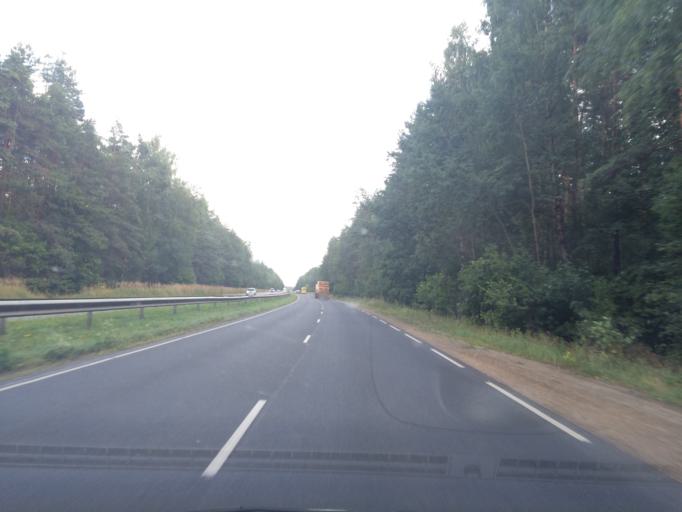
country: LV
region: Kekava
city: Kekava
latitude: 56.8654
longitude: 24.2858
